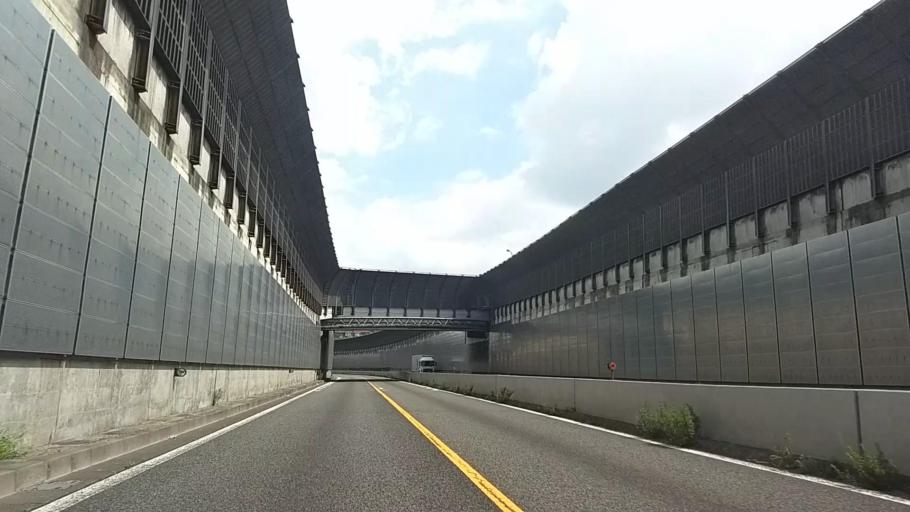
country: JP
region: Tokyo
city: Hachioji
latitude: 35.6269
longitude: 139.3479
